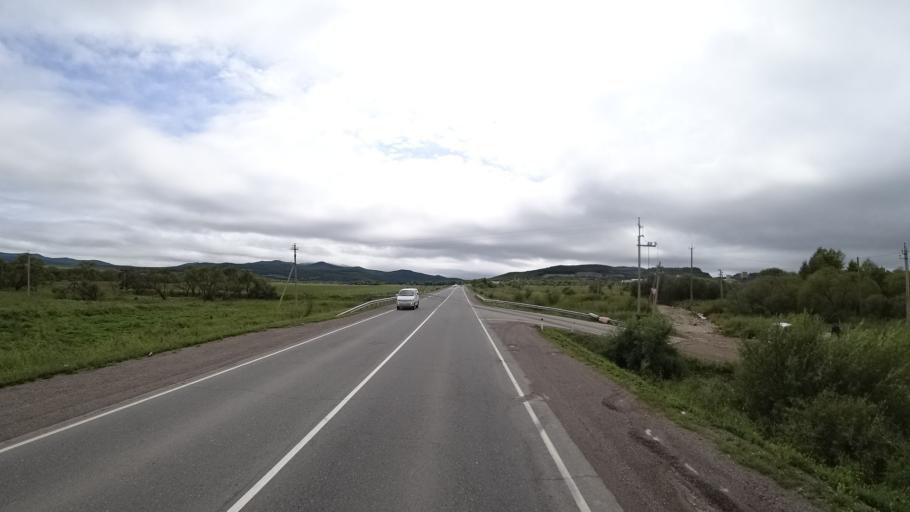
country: RU
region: Primorskiy
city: Monastyrishche
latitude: 44.1766
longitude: 132.4414
